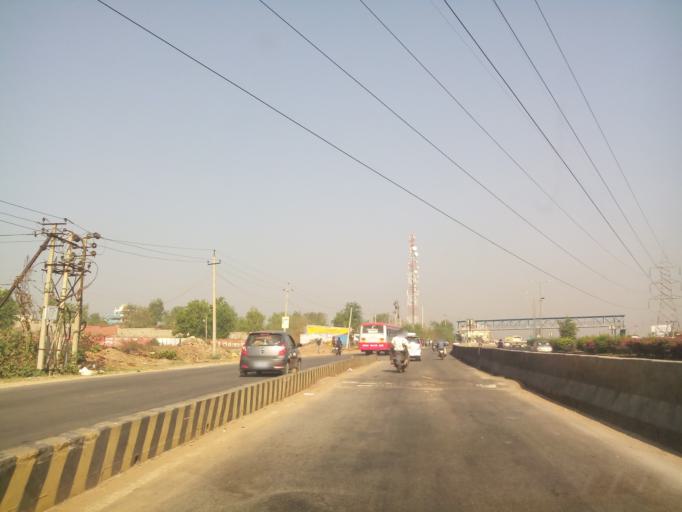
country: IN
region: Karnataka
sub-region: Bangalore Rural
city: Nelamangala
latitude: 13.0941
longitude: 77.3906
